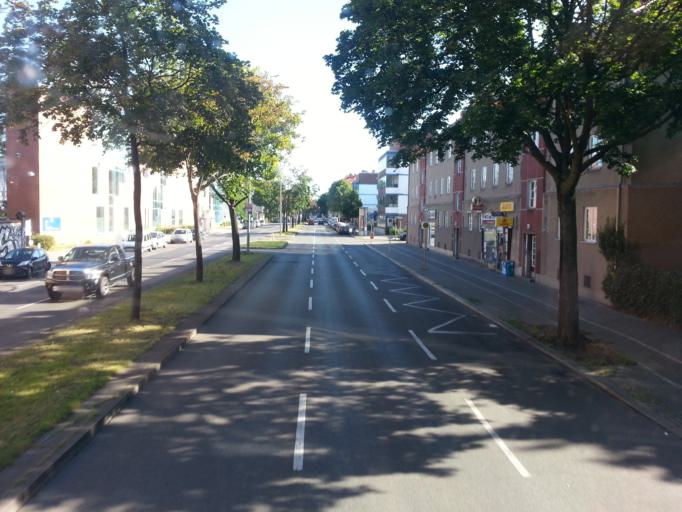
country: DE
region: Berlin
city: Reinickendorf
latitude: 52.5718
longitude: 13.3308
